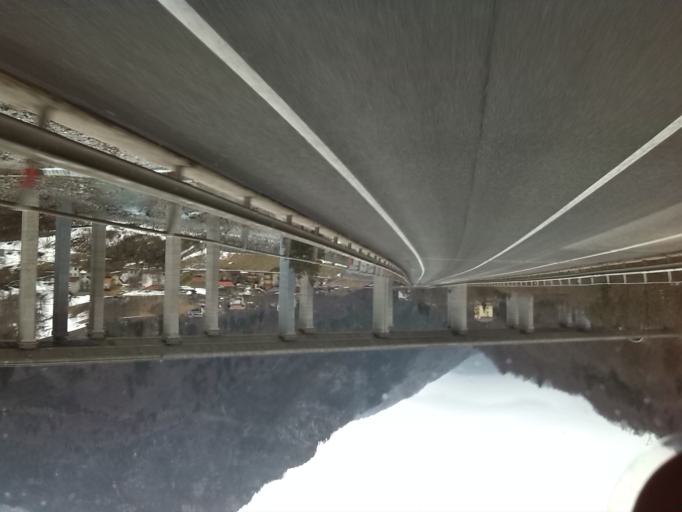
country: IT
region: Friuli Venezia Giulia
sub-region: Provincia di Udine
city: Pontebba
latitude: 46.4744
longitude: 13.2939
